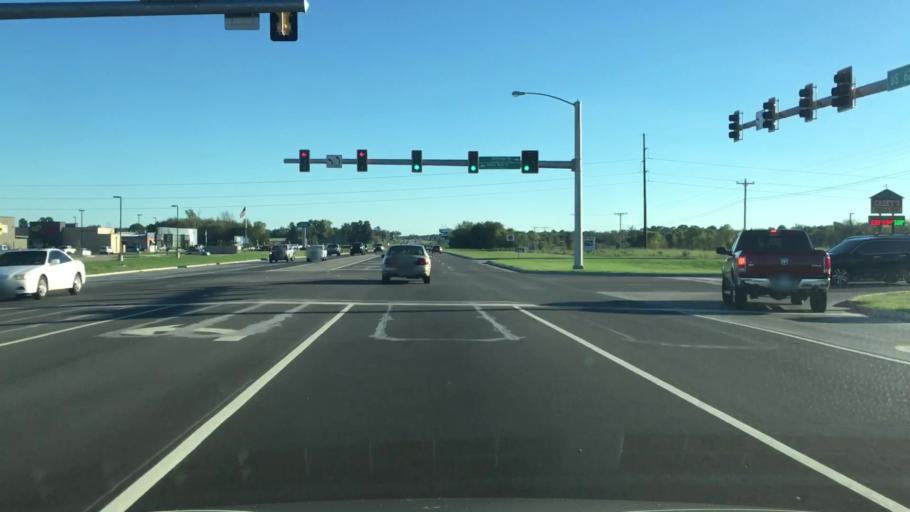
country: US
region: Oklahoma
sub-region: Cherokee County
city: Park Hill
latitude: 35.8775
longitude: -94.9763
